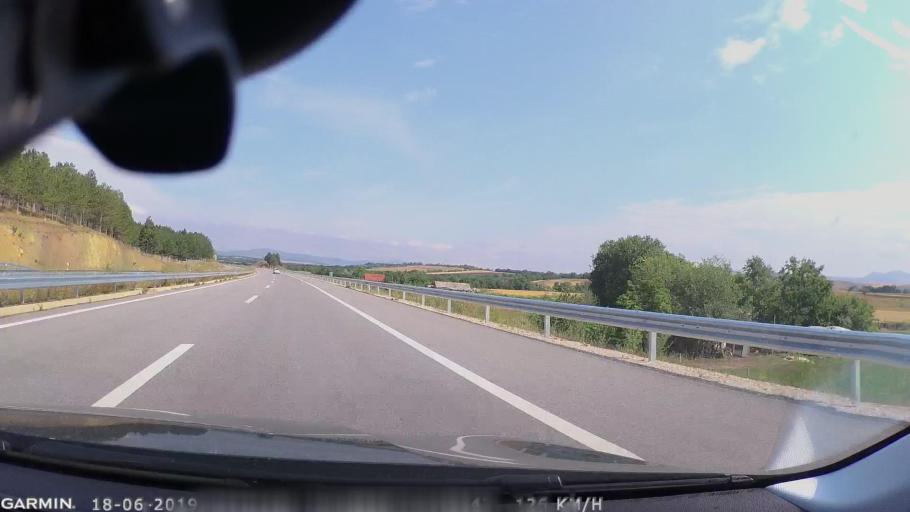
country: MK
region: Sveti Nikole
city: Sveti Nikole
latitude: 41.8859
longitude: 21.9330
